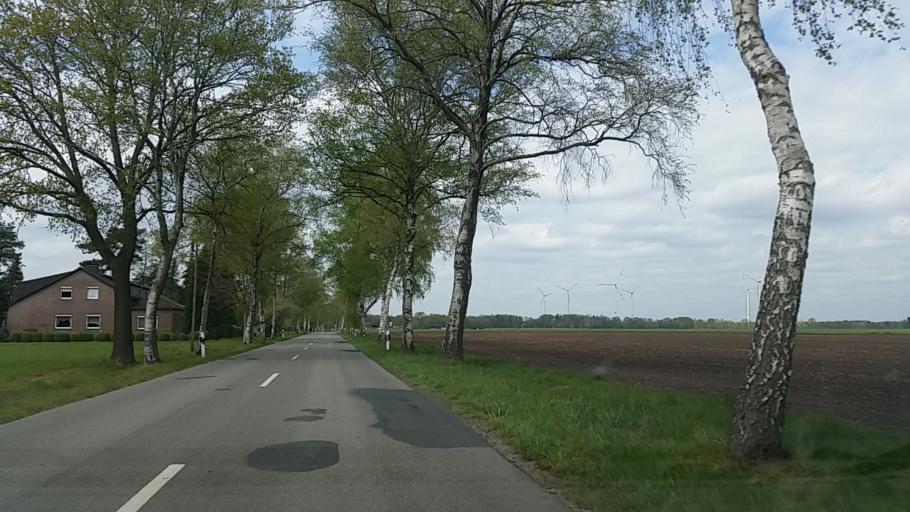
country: DE
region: Lower Saxony
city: Otter
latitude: 53.1947
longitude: 9.7226
